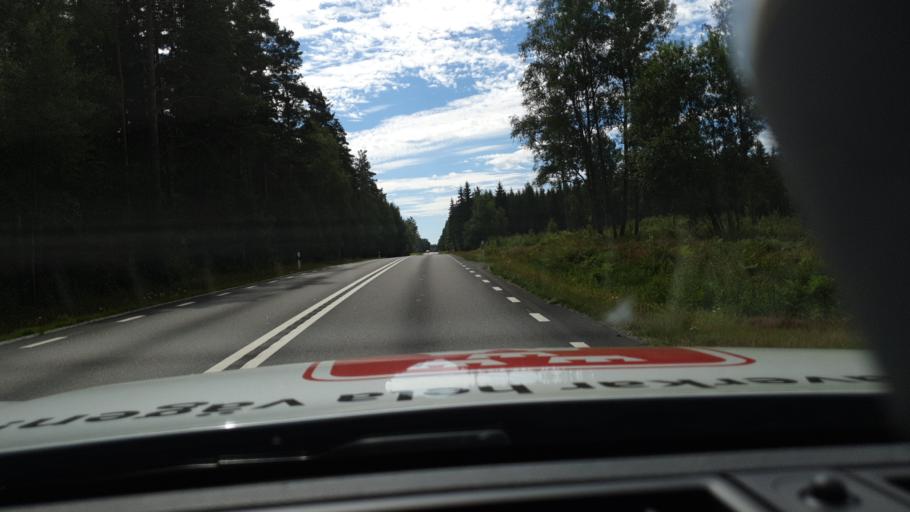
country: SE
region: Joenkoeping
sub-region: Savsjo Kommun
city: Stockaryd
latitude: 57.3000
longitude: 14.5212
